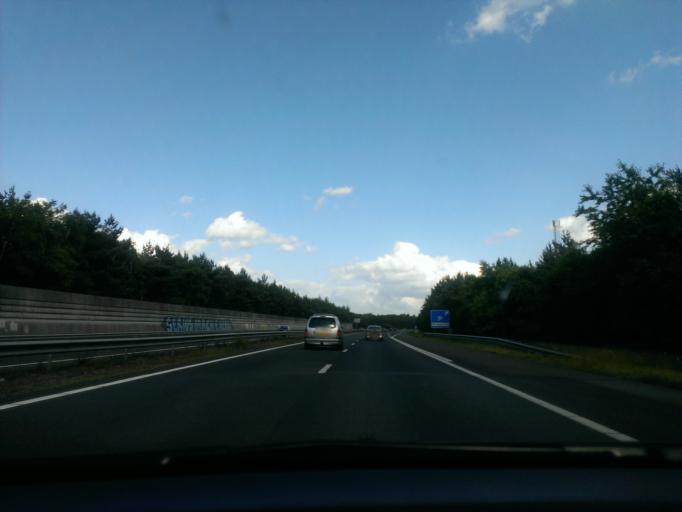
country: NL
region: Gelderland
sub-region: Gemeente Apeldoorn
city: Beekbergen
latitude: 52.1792
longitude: 5.9349
